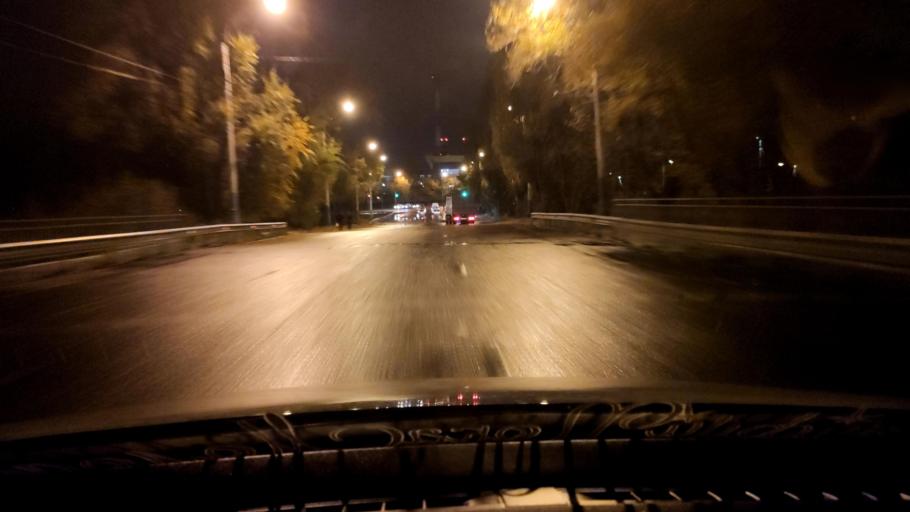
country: RU
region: Voronezj
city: Maslovka
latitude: 51.6233
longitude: 39.2362
